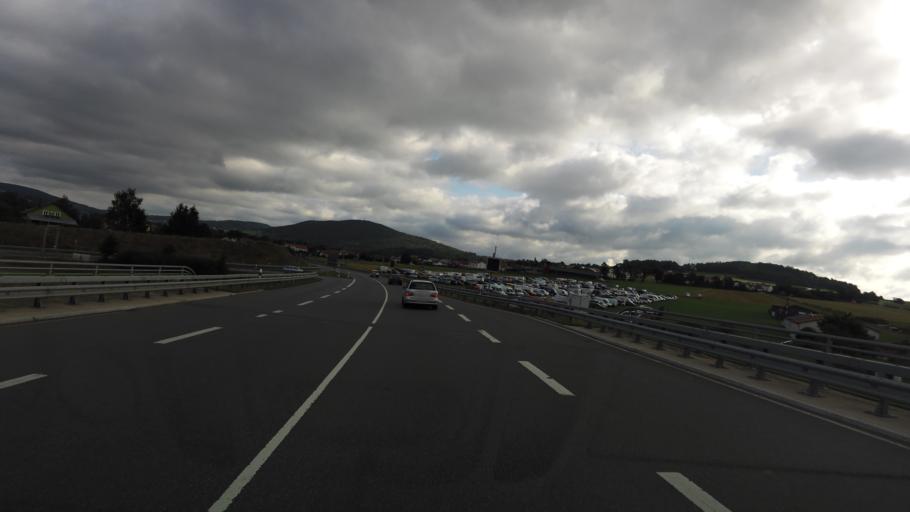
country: DE
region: Bavaria
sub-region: Upper Palatinate
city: Furth im Wald
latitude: 49.3010
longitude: 12.8517
